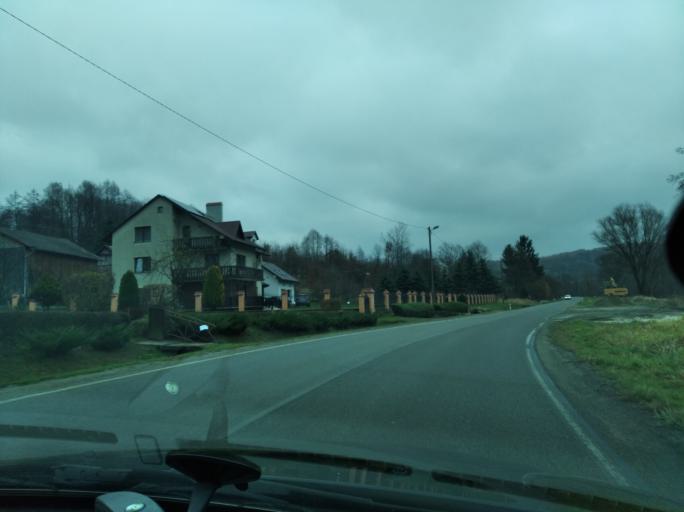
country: PL
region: Subcarpathian Voivodeship
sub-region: Powiat przeworski
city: Manasterz
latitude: 49.9226
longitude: 22.3105
